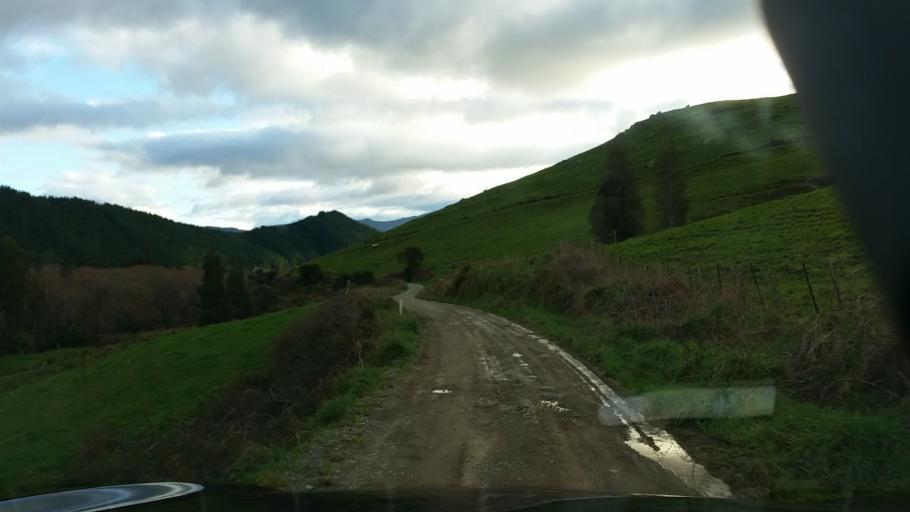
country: NZ
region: Nelson
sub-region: Nelson City
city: Nelson
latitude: -41.2085
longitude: 173.6355
